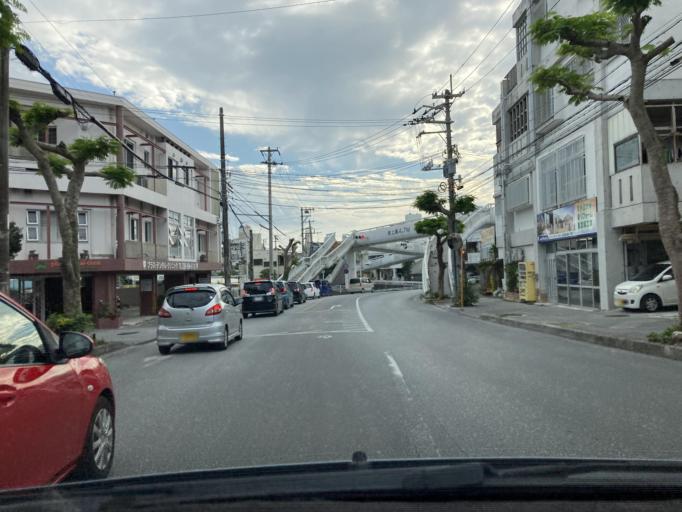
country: JP
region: Okinawa
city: Naha-shi
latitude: 26.2163
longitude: 127.7255
